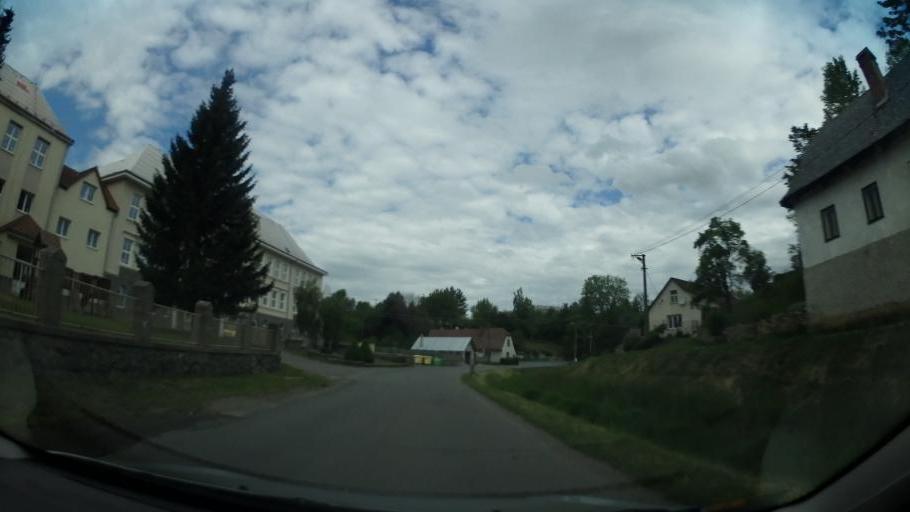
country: CZ
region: Pardubicky
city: Kuncina
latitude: 49.8331
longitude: 16.7019
